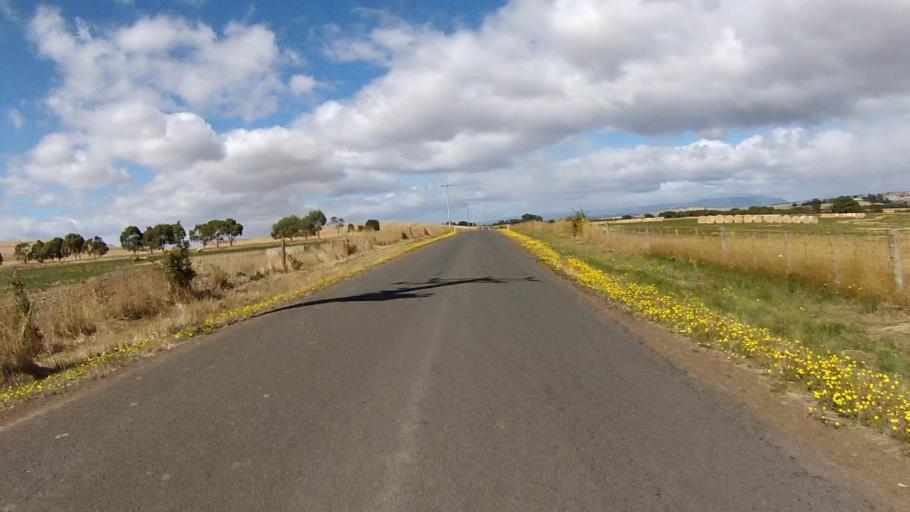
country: AU
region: Tasmania
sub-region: Northern Midlands
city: Evandale
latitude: -41.7626
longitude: 147.4838
